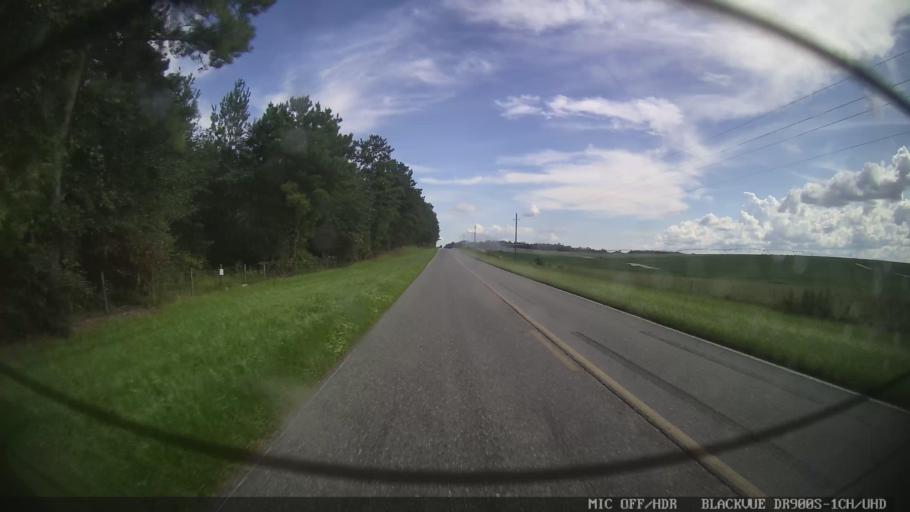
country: US
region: Florida
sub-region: Madison County
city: Madison
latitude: 30.5903
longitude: -83.2242
